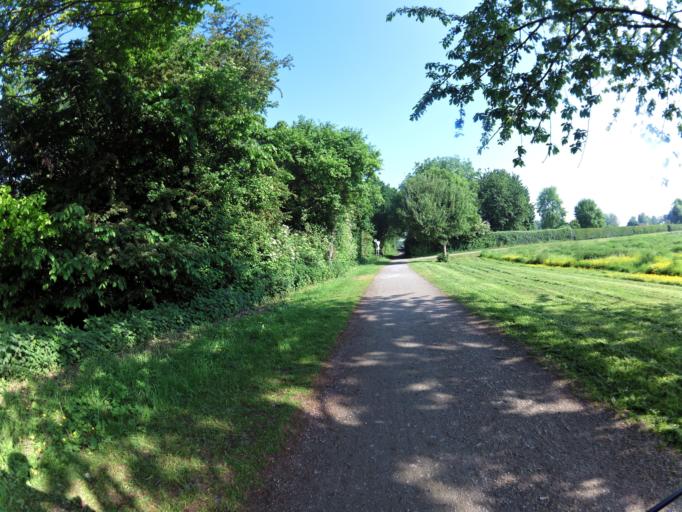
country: DE
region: North Rhine-Westphalia
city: Julich
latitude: 50.9310
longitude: 6.3466
